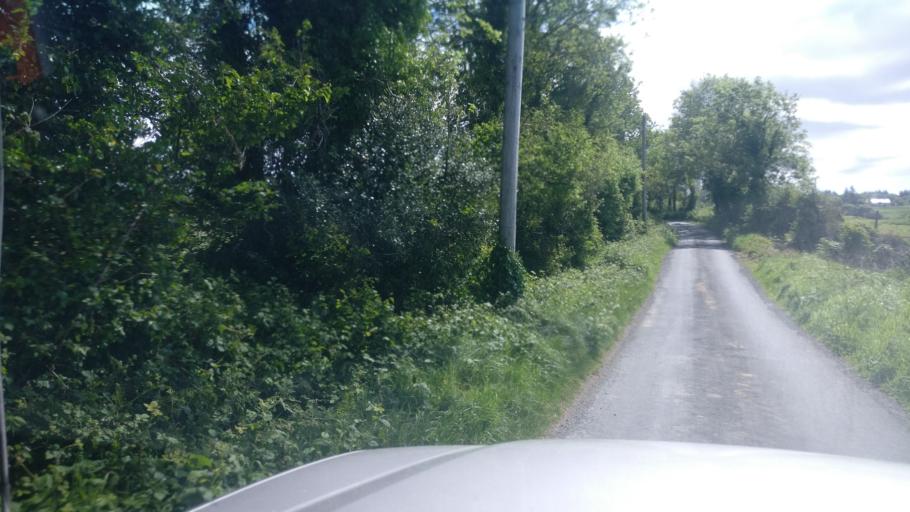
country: IE
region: Connaught
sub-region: County Galway
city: Gort
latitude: 53.1352
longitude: -8.7137
